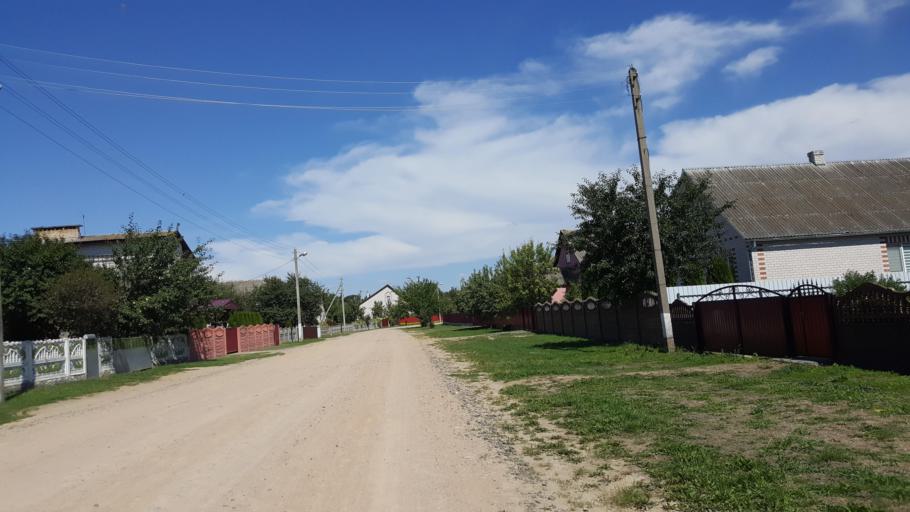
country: BY
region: Brest
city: Charnawchytsy
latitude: 52.2644
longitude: 23.5827
